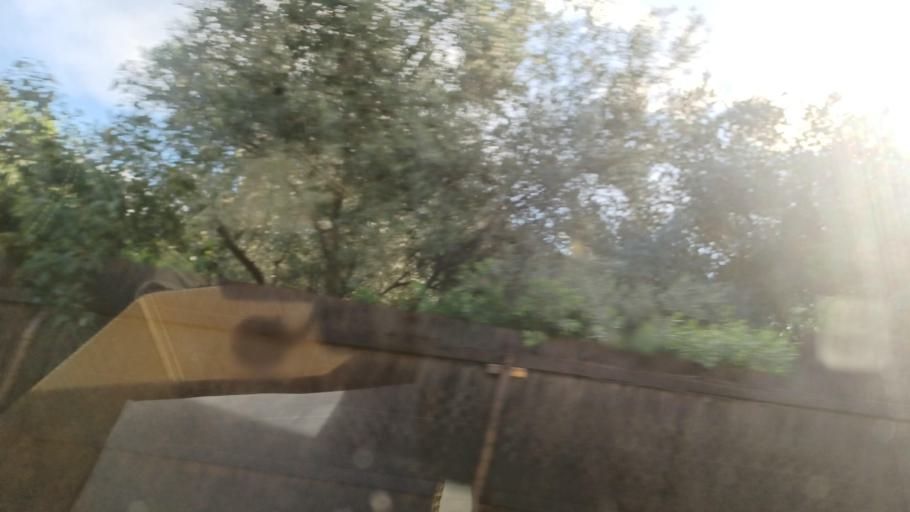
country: CY
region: Lefkosia
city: Lythrodontas
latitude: 34.9271
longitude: 33.2977
